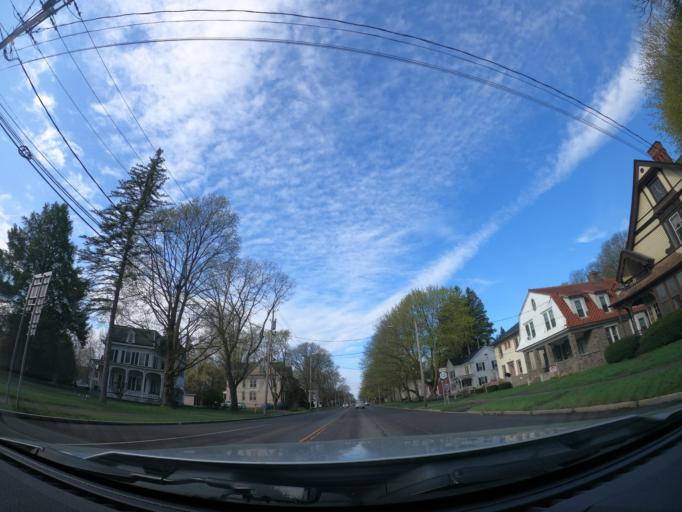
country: US
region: New York
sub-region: Cortland County
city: Cortland
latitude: 42.5949
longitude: -76.1847
